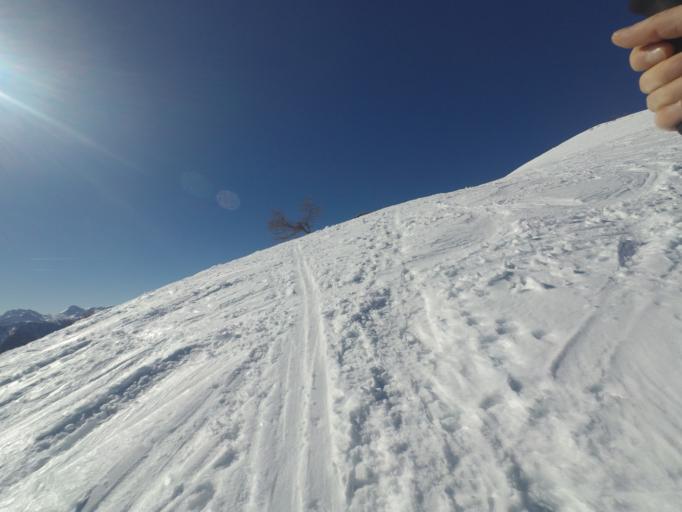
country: AT
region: Upper Austria
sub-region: Politischer Bezirk Gmunden
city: Sankt Wolfgang im Salzkammergut
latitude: 47.6658
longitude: 13.3787
